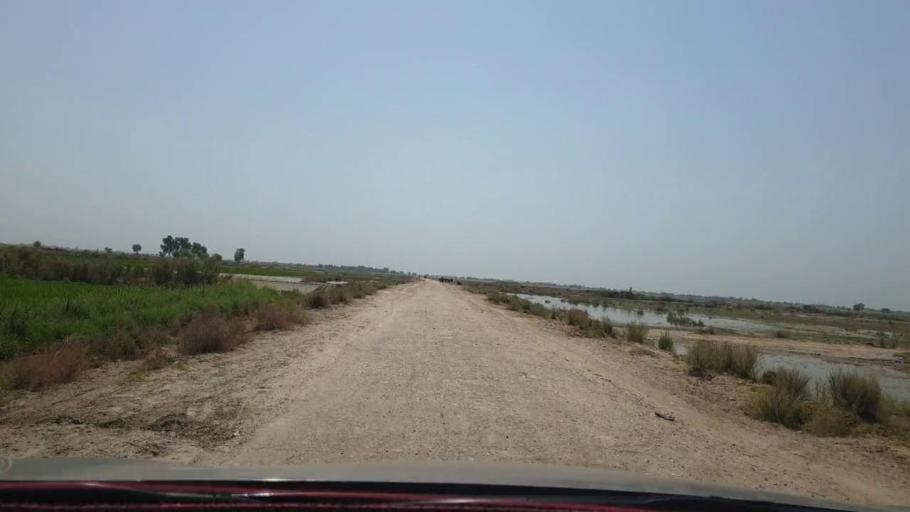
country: PK
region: Sindh
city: Kambar
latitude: 27.5835
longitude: 67.8768
